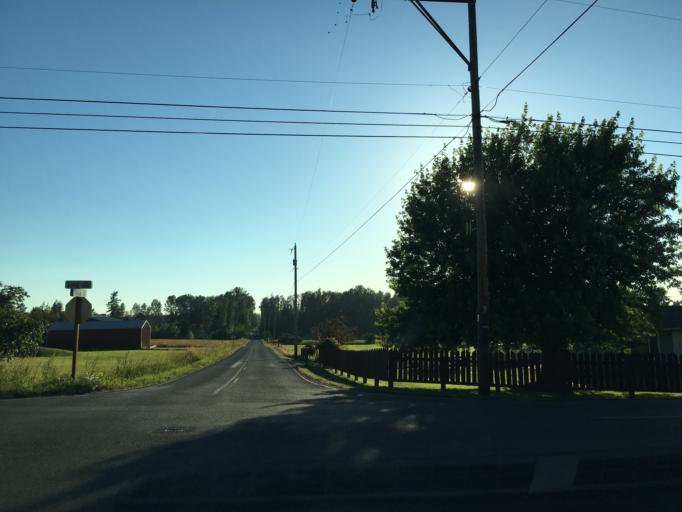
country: US
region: Washington
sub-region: Whatcom County
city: Sudden Valley
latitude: 48.8181
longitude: -122.3324
